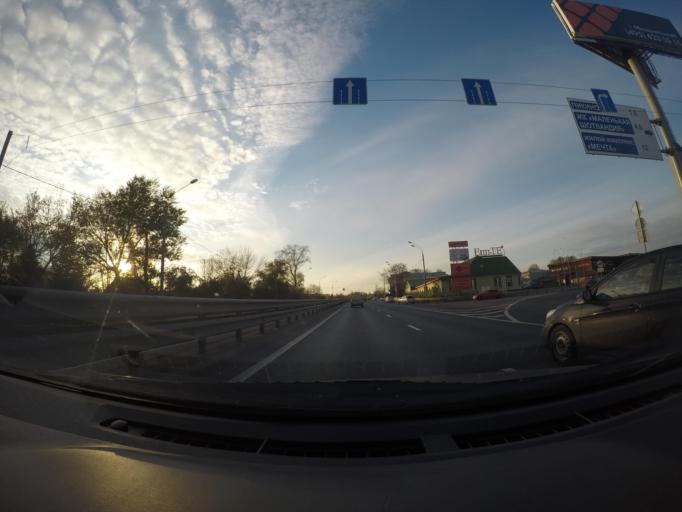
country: RU
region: Moskovskaya
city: Skhodnya
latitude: 55.9748
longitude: 37.3102
